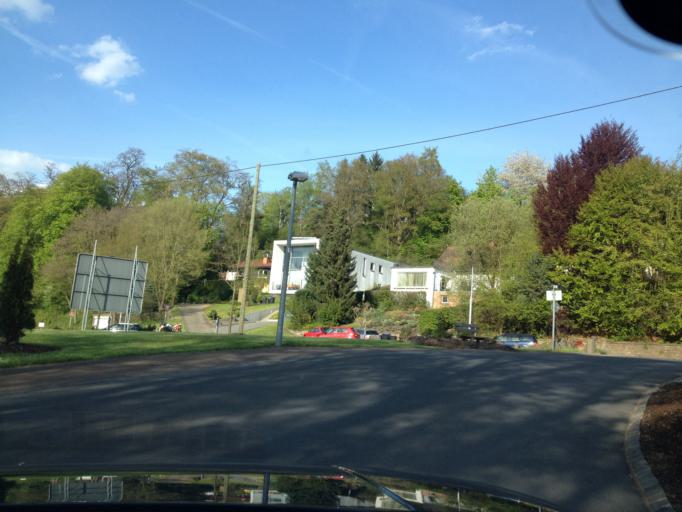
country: DE
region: Saarland
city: Sankt Wendel
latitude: 49.4711
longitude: 7.1753
